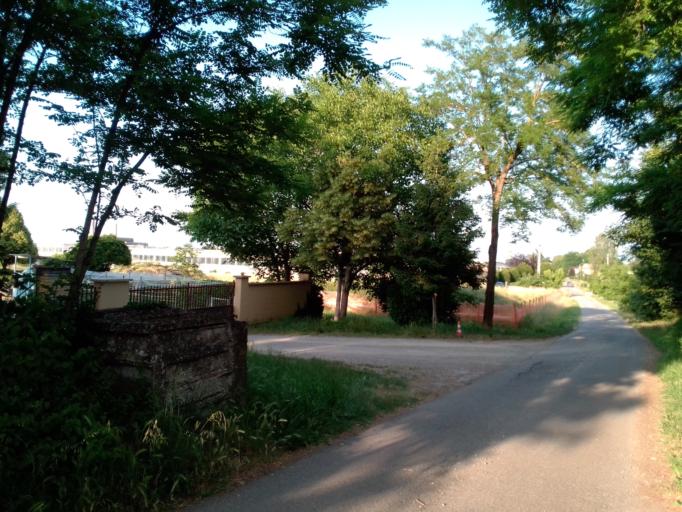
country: IT
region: Emilia-Romagna
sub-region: Provincia di Piacenza
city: Borgonovo Valtidone
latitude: 45.0073
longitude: 9.4383
